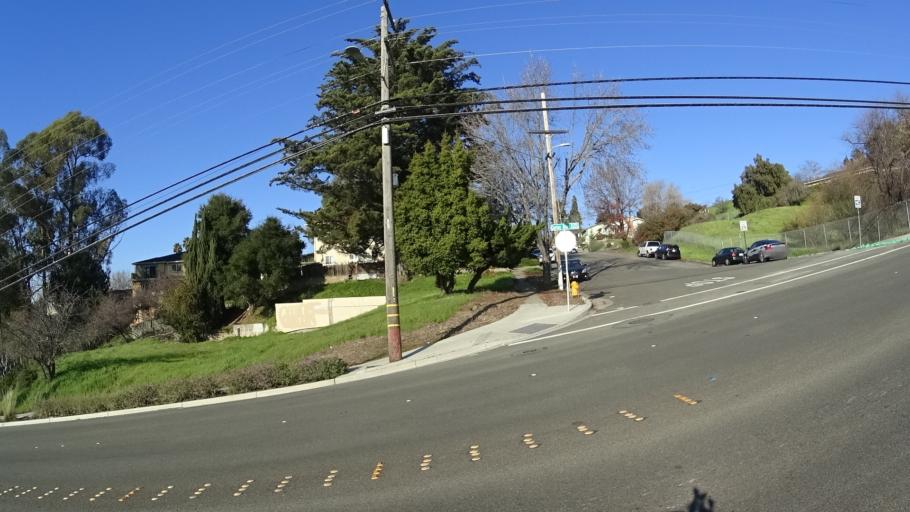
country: US
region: California
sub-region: Alameda County
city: Hayward
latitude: 37.6612
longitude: -122.0701
